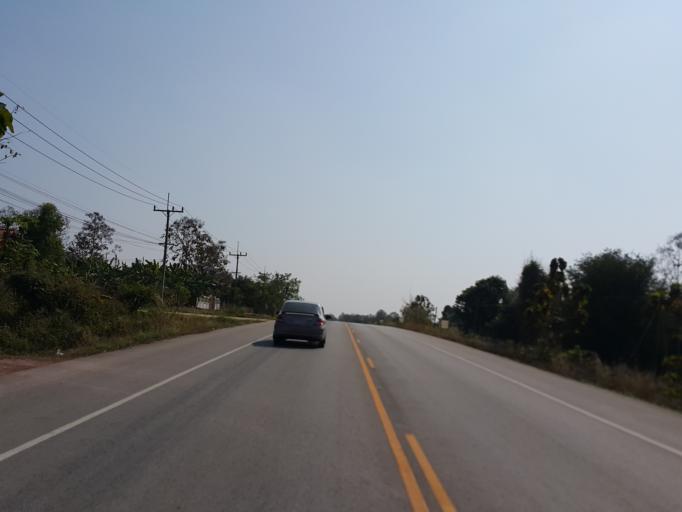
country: TH
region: Lampang
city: Wang Nuea
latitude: 18.9800
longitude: 99.6095
